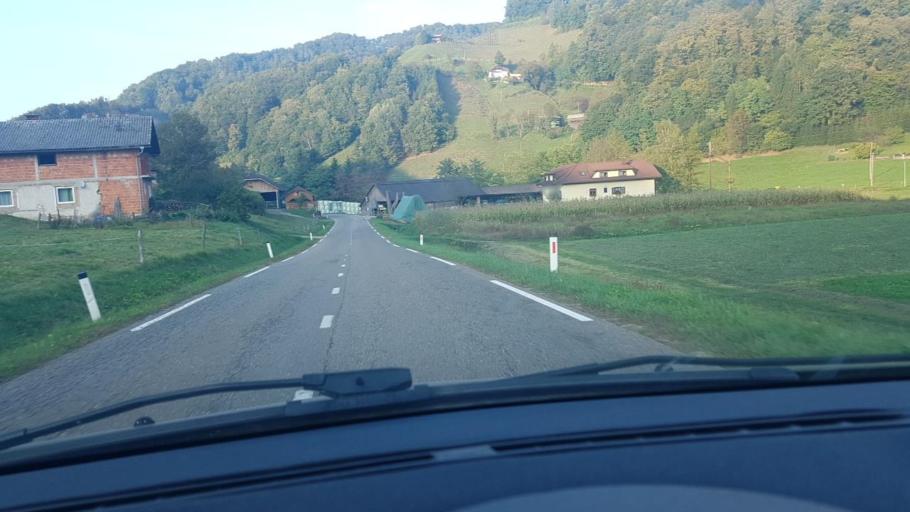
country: SI
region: Makole
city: Makole
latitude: 46.2938
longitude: 15.7204
